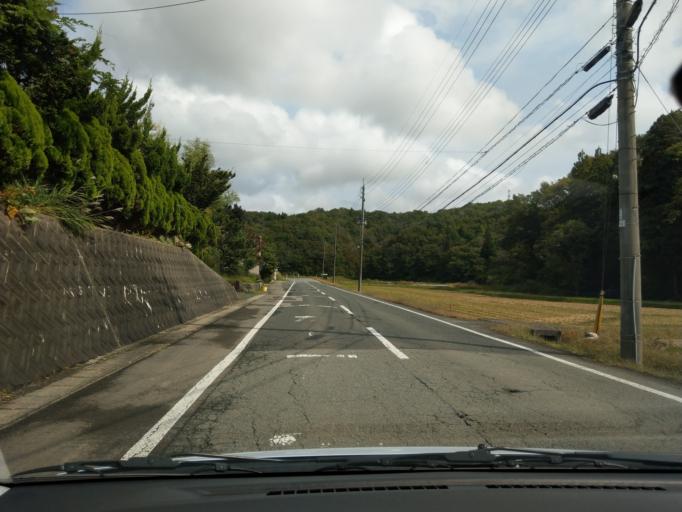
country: JP
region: Akita
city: Omagari
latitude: 39.5017
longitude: 140.3107
